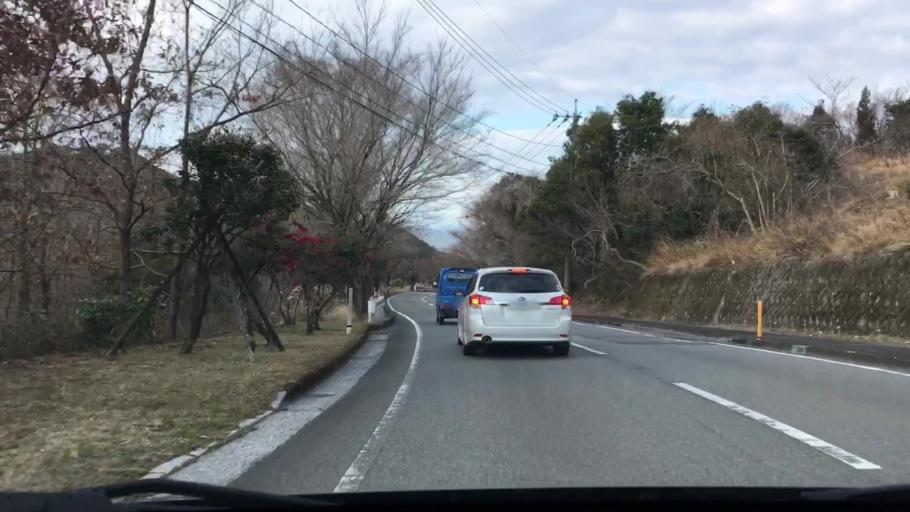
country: JP
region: Miyazaki
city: Miyazaki-shi
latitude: 31.8060
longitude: 131.3022
